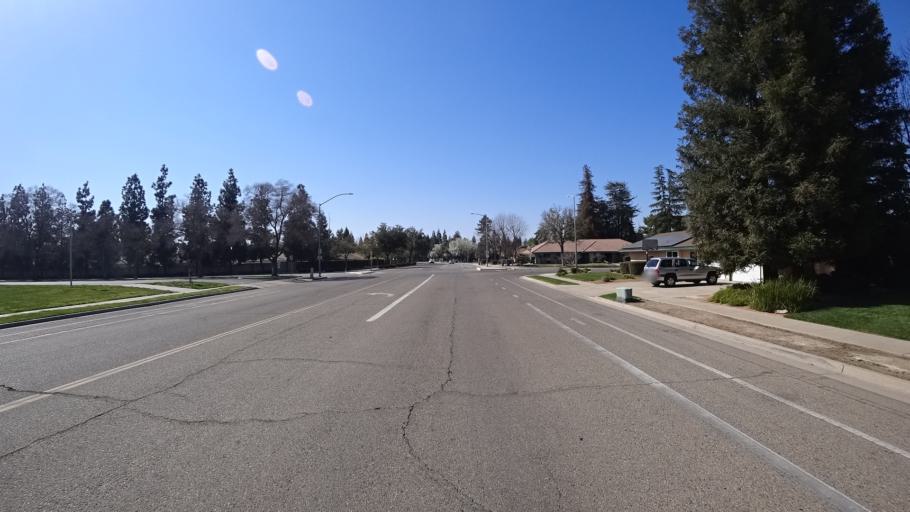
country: US
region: California
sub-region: Fresno County
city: Fresno
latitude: 36.8300
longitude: -119.8529
